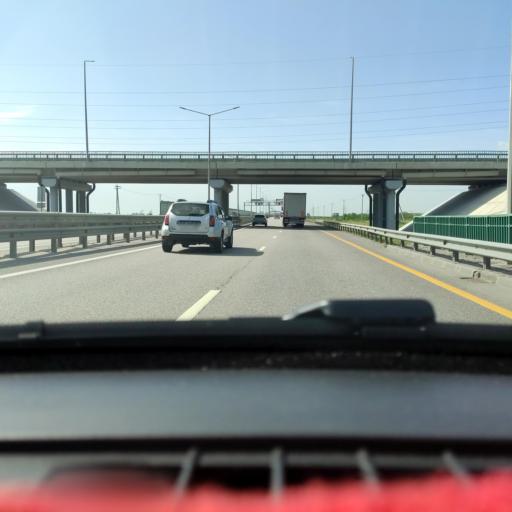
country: RU
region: Voronezj
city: Novaya Usman'
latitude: 51.6287
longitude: 39.3184
